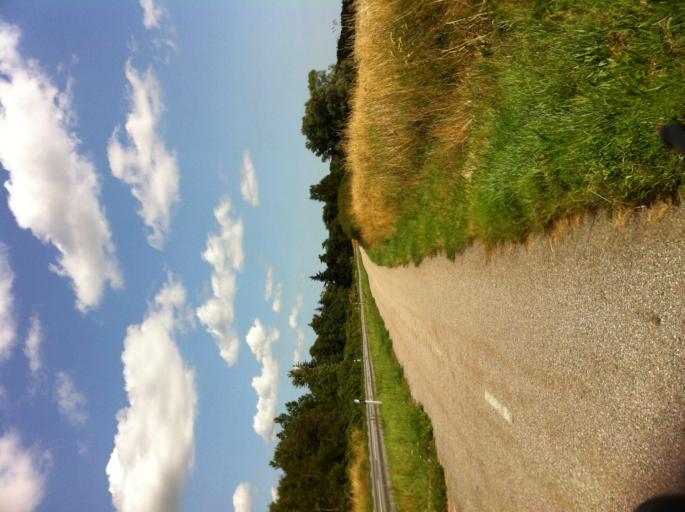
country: SE
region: Skane
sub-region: Ystads Kommun
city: Ystad
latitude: 55.4268
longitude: 13.7580
